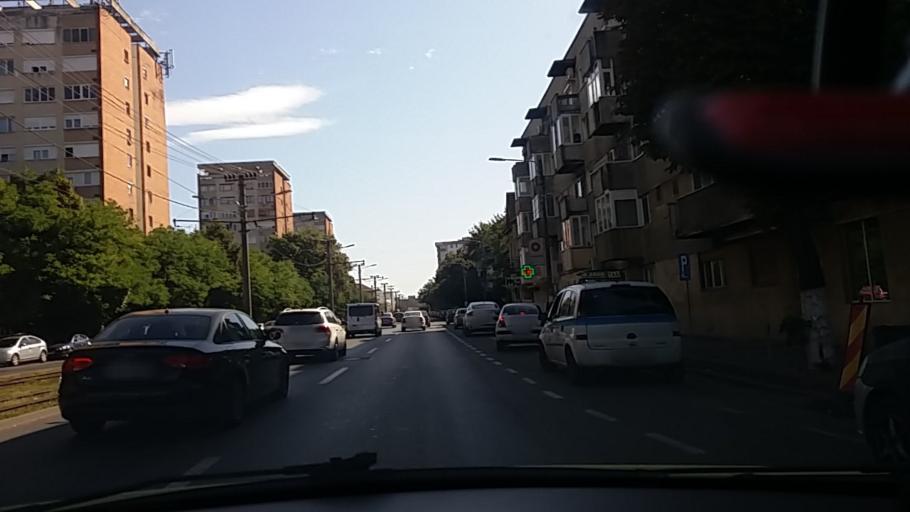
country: RO
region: Arad
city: Arad
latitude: 46.1823
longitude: 21.3255
